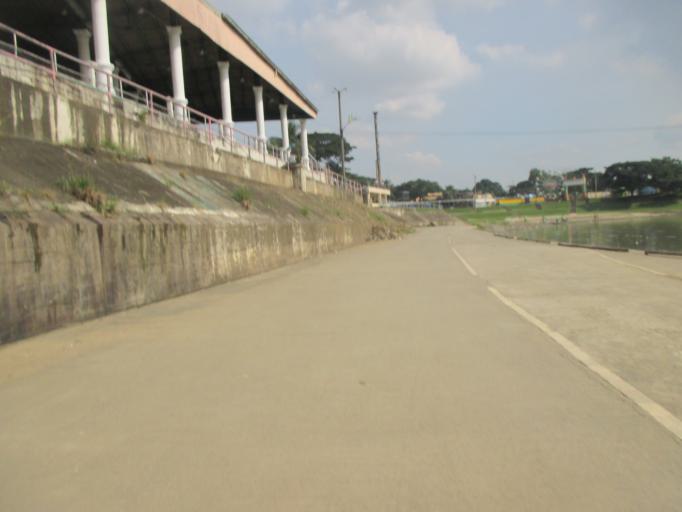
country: PH
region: Metro Manila
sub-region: Marikina
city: Calumpang
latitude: 14.6296
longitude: 121.0829
